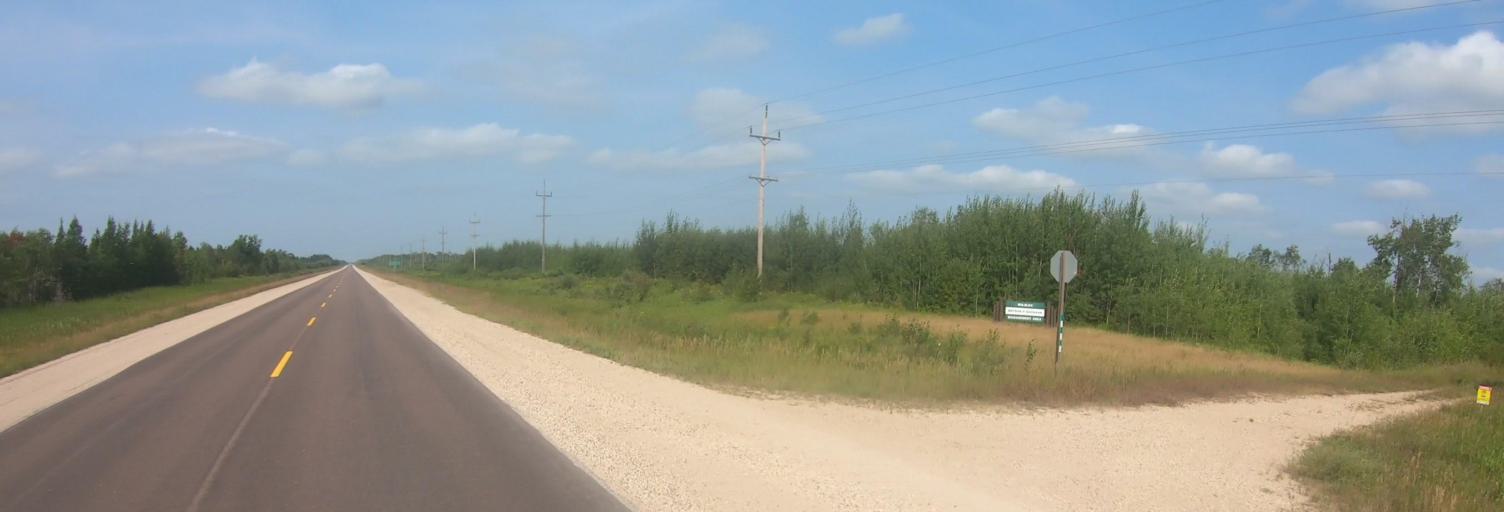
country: CA
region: Manitoba
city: La Broquerie
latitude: 49.2671
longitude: -96.3745
